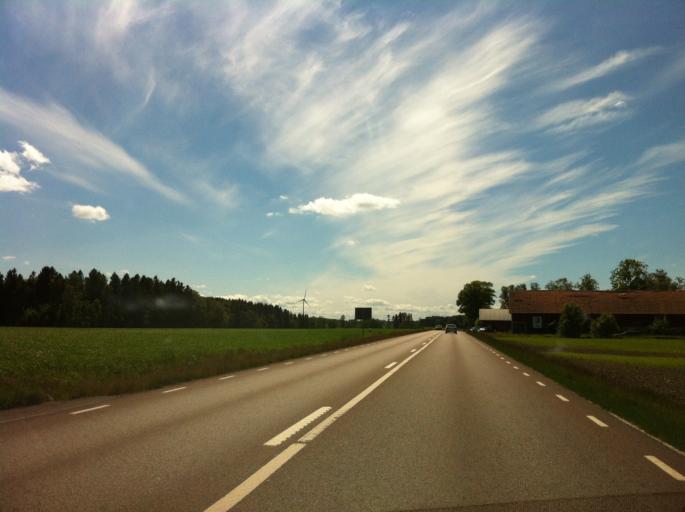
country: SE
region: Vaestra Goetaland
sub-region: Vanersborgs Kommun
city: Bralanda
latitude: 58.5542
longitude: 12.3519
